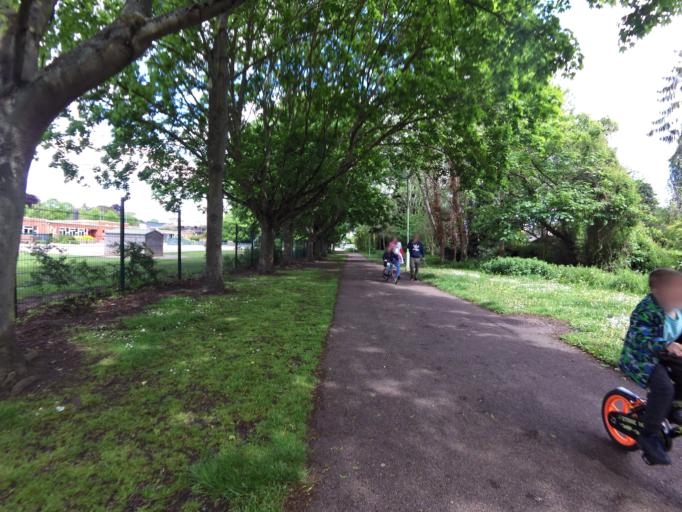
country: GB
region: England
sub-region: Suffolk
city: Bury St Edmunds
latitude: 52.2388
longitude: 0.7019
